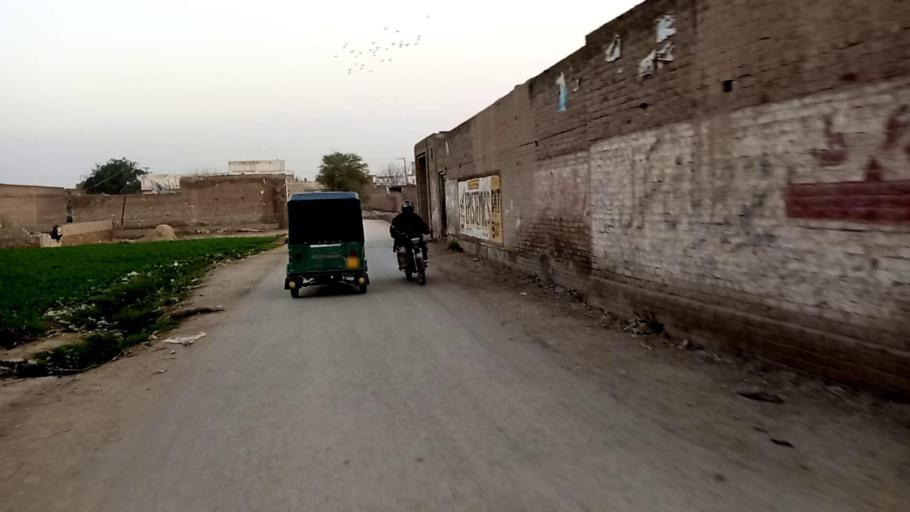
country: PK
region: Khyber Pakhtunkhwa
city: Peshawar
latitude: 34.0306
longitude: 71.4949
